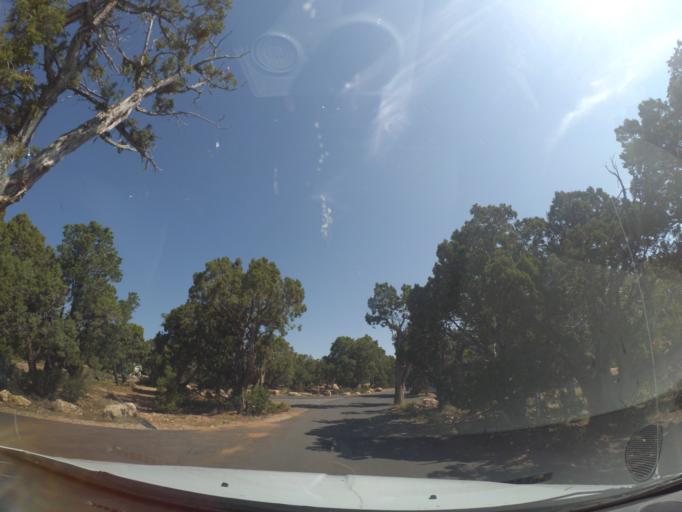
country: US
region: Arizona
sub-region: Coconino County
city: Grand Canyon
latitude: 36.0384
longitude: -111.8229
